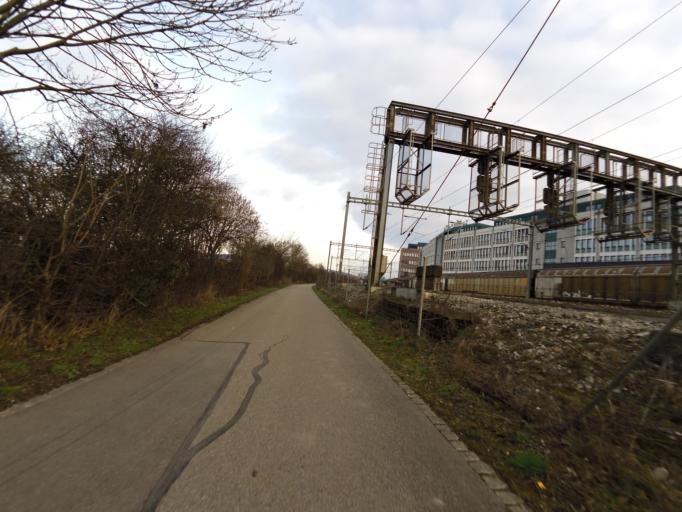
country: CH
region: Zurich
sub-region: Bezirk Dietikon
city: Schlieren / Boden
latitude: 47.4001
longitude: 8.4574
